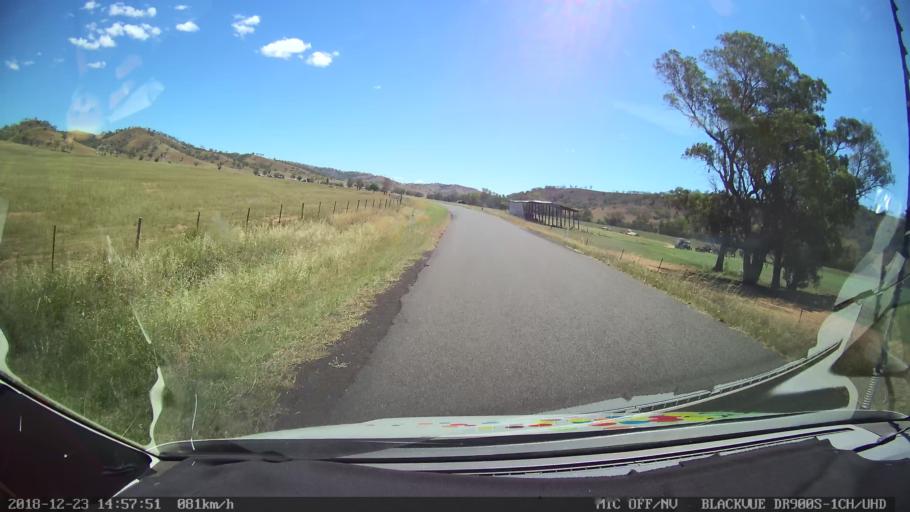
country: AU
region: New South Wales
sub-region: Tamworth Municipality
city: Manilla
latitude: -30.7119
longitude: 150.8194
